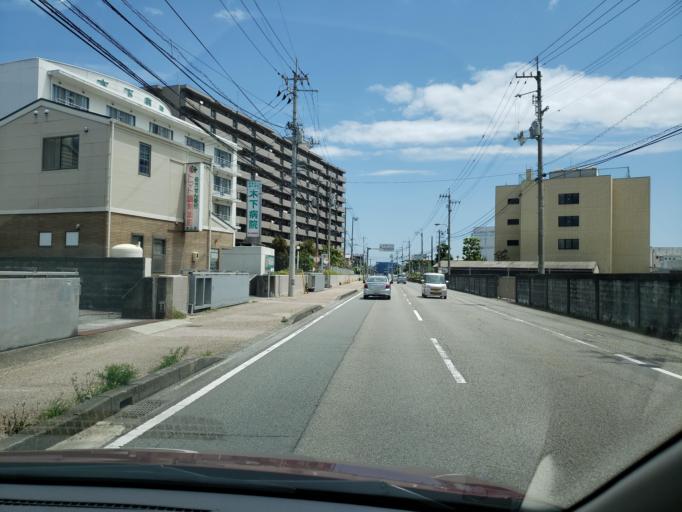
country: JP
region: Tokushima
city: Tokushima-shi
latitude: 34.0600
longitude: 134.5753
